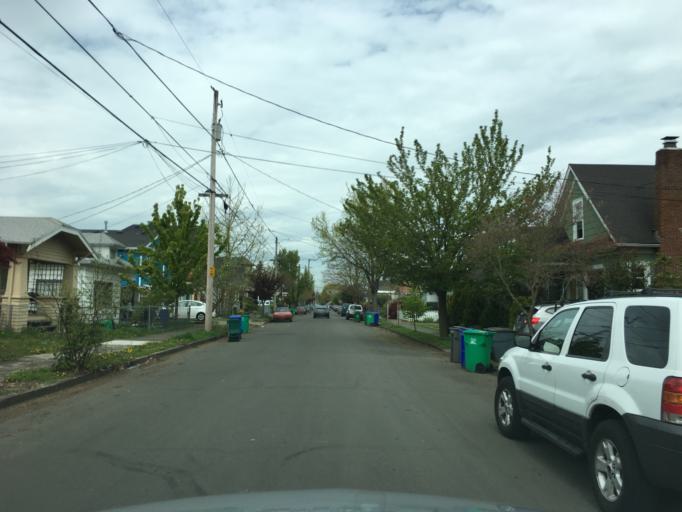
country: US
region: Oregon
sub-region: Multnomah County
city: Lents
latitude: 45.5247
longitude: -122.5823
